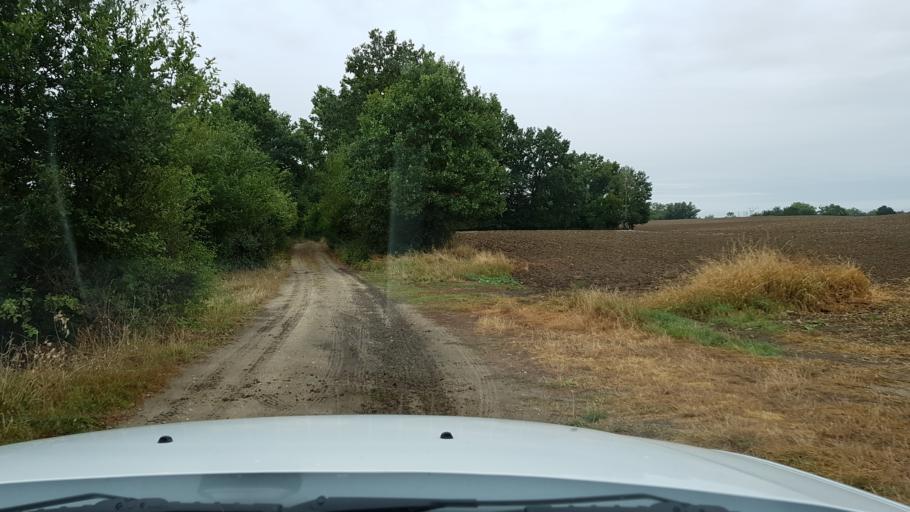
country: PL
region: West Pomeranian Voivodeship
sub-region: Powiat gryfinski
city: Chojna
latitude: 52.8987
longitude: 14.4504
